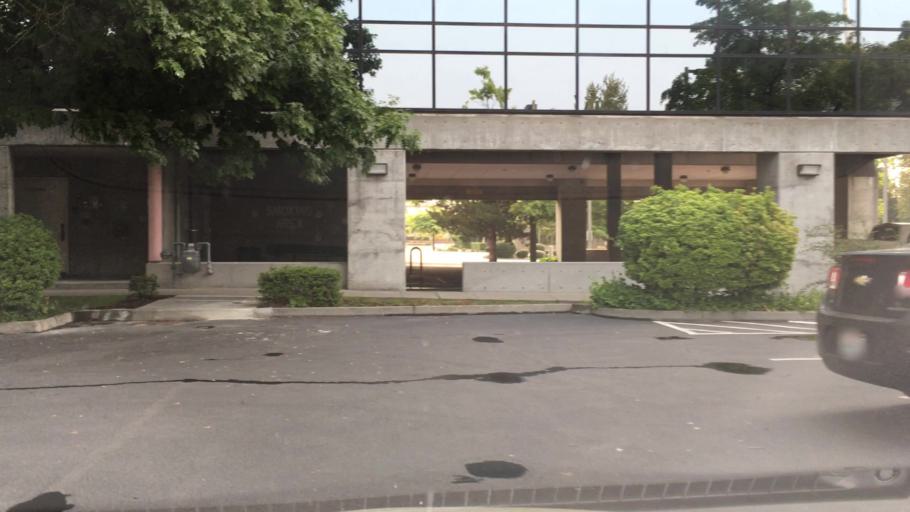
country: US
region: Washington
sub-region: Snohomish County
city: Mill Creek
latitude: 47.9091
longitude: -122.2209
